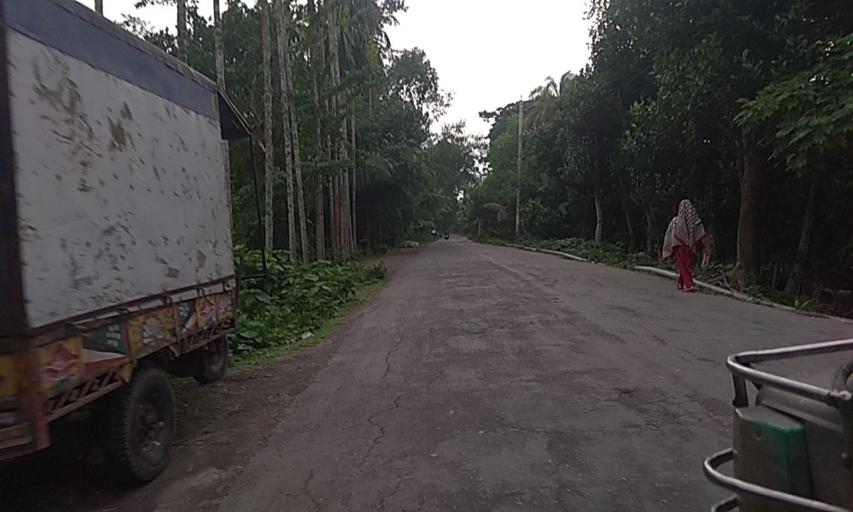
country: BD
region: Dhaka
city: Dohar
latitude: 23.4604
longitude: 89.9891
